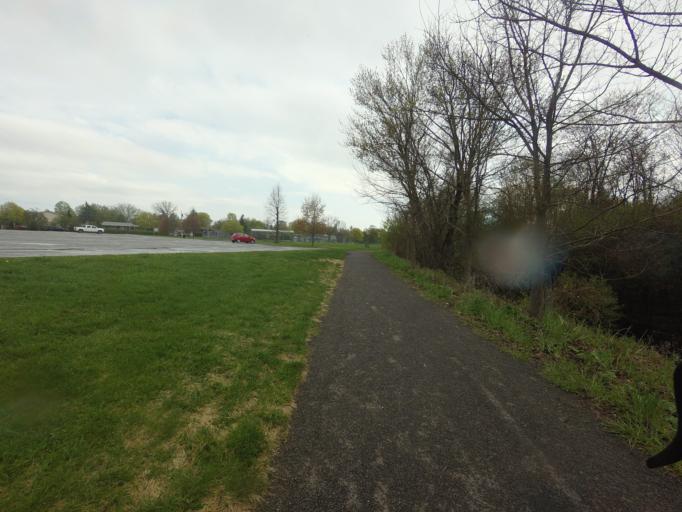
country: CA
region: Ontario
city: Carleton Place
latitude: 45.1427
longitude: -76.1397
